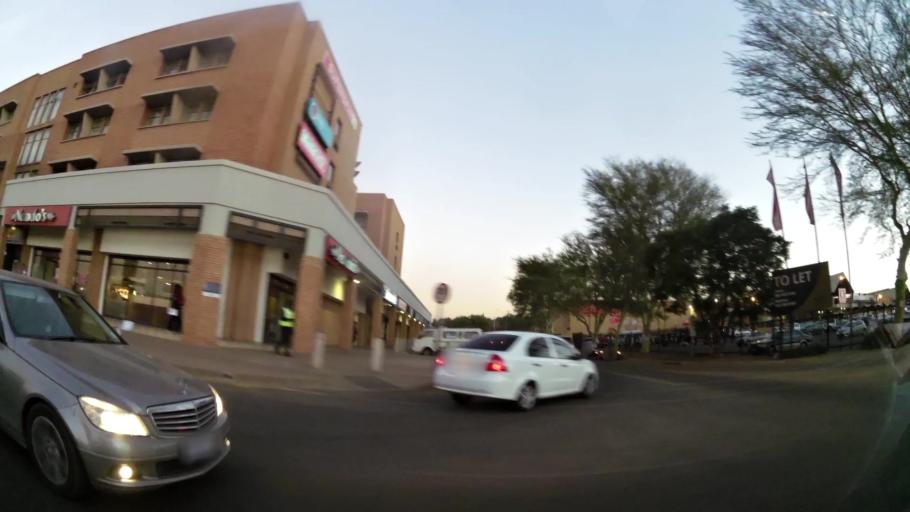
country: ZA
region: Gauteng
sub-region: City of Tshwane Metropolitan Municipality
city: Pretoria
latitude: -25.7333
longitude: 28.3031
